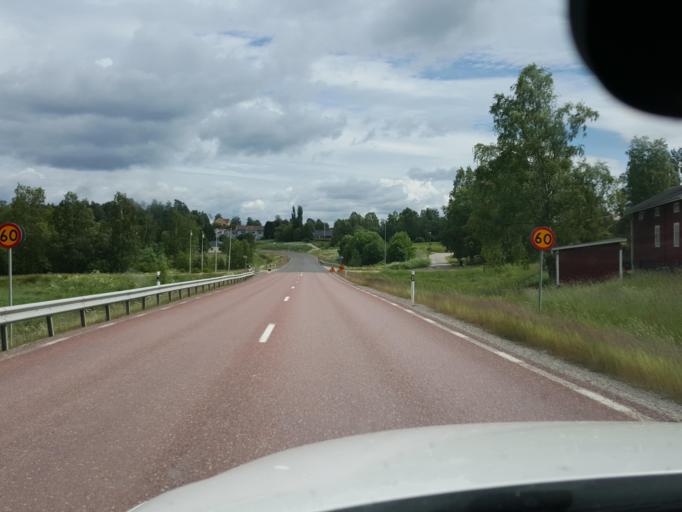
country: SE
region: Gaevleborg
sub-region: Ljusdals Kommun
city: Farila
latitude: 61.7983
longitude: 15.8238
